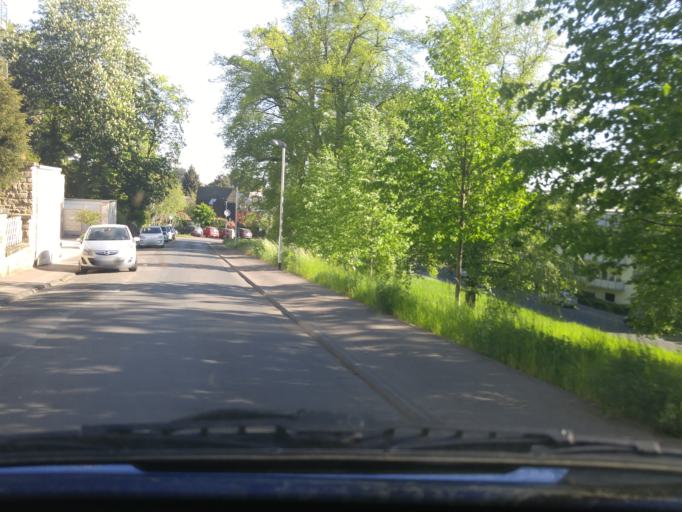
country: DE
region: Hesse
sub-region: Regierungsbezirk Darmstadt
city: Bad Nauheim
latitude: 50.3662
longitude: 8.7327
